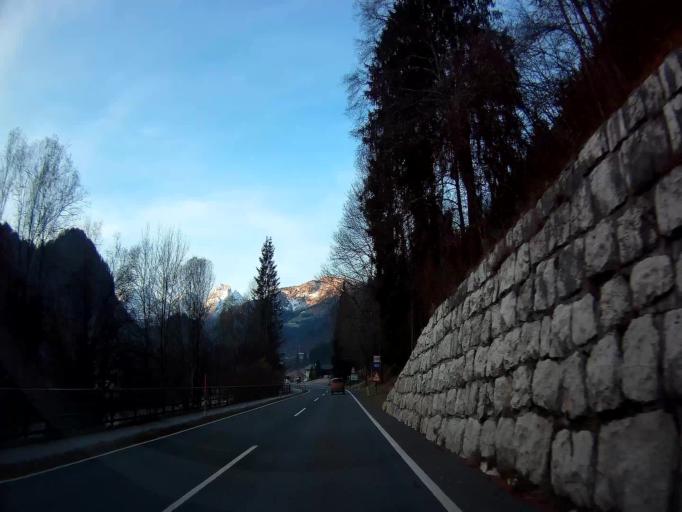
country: AT
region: Salzburg
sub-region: Politischer Bezirk Zell am See
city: Unken
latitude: 47.6289
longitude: 12.7240
